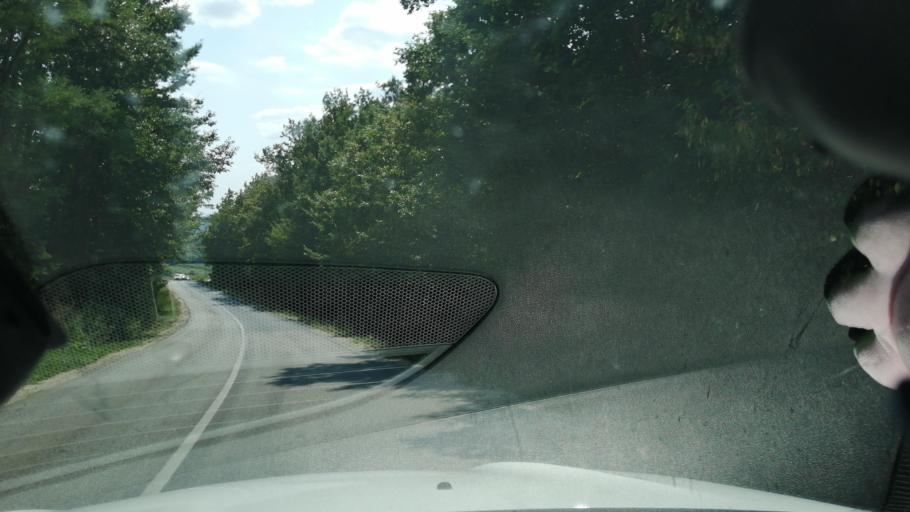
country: RS
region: Central Serbia
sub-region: Moravicki Okrug
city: Cacak
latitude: 43.8137
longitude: 20.2759
